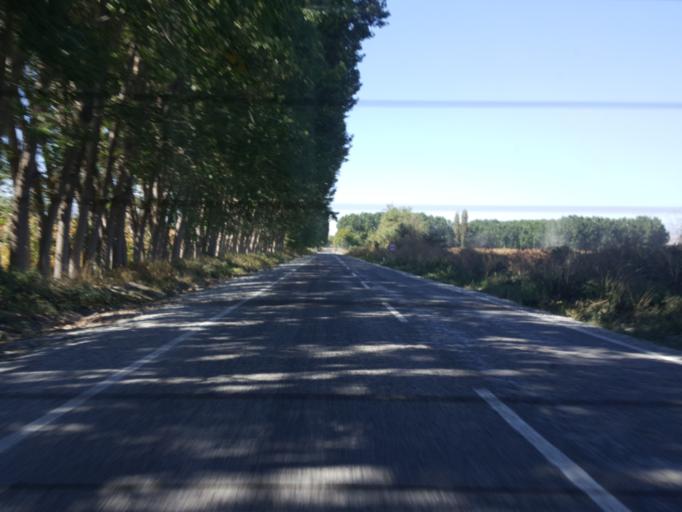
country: TR
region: Tokat
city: Pazar
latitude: 40.2699
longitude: 36.2356
